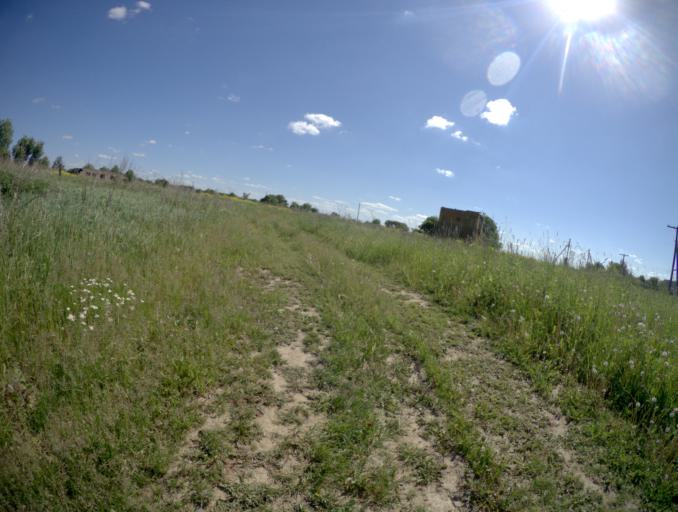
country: RU
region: Ivanovo
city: Gavrilov Posad
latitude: 56.5255
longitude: 40.2174
